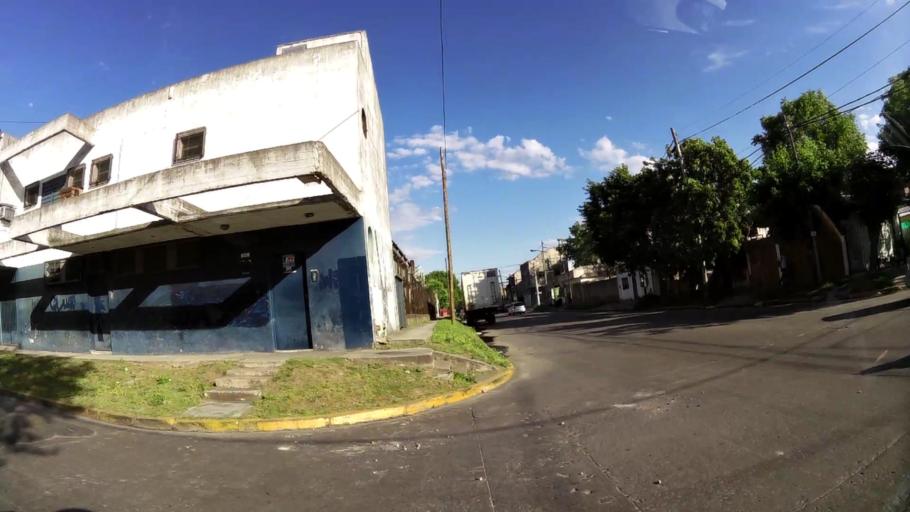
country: AR
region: Buenos Aires
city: Hurlingham
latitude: -34.5647
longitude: -58.6172
